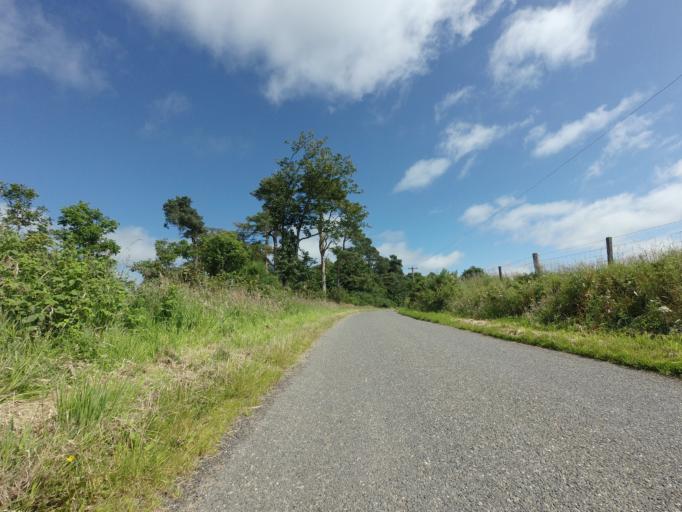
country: GB
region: Scotland
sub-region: Aberdeenshire
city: Turriff
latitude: 57.5839
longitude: -2.5060
